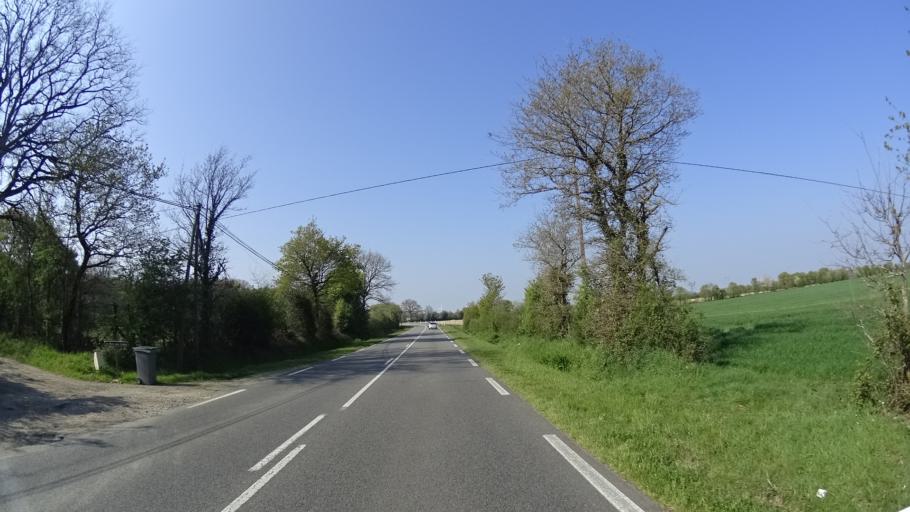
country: FR
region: Pays de la Loire
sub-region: Departement de la Loire-Atlantique
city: Sainte-Pazanne
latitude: 47.0932
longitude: -1.8305
